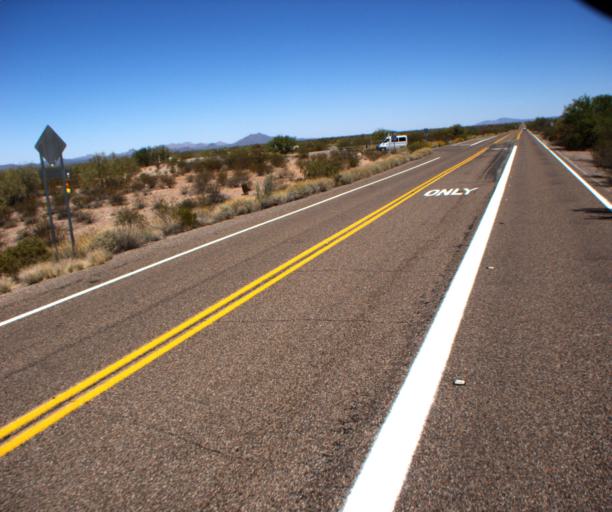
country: US
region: Arizona
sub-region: Pima County
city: Ajo
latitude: 32.1291
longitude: -112.7678
